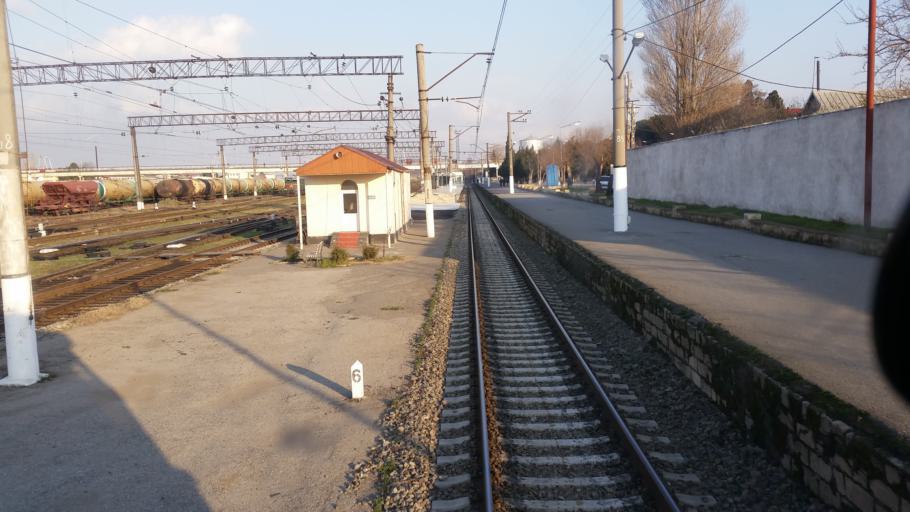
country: AZ
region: Baki
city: Bilajari
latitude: 40.4328
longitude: 49.8016
